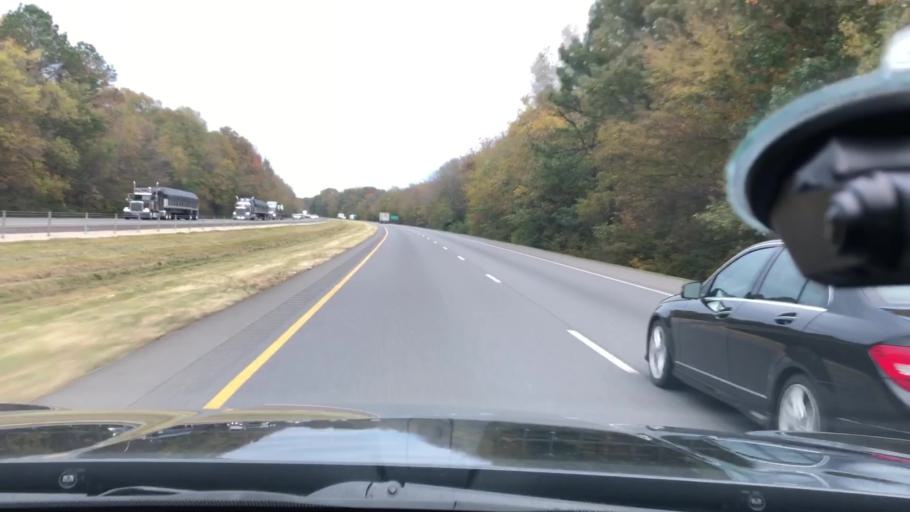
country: US
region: Arkansas
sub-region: Hot Spring County
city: Malvern
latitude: 34.3679
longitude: -92.8637
